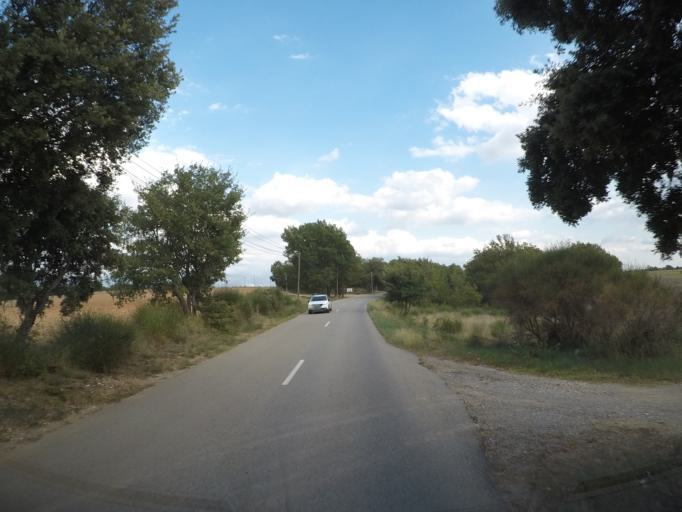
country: FR
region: Provence-Alpes-Cote d'Azur
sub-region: Departement des Alpes-de-Haute-Provence
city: Valensole
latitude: 43.8348
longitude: 6.0202
